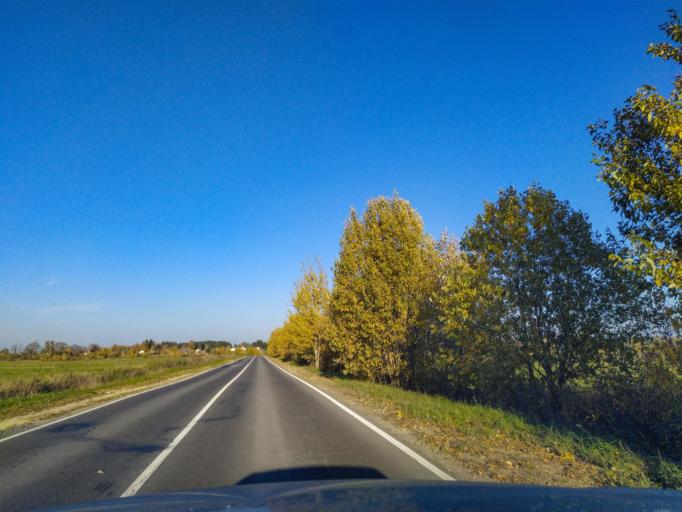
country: RU
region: Leningrad
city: Siverskiy
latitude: 59.3180
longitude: 30.0359
